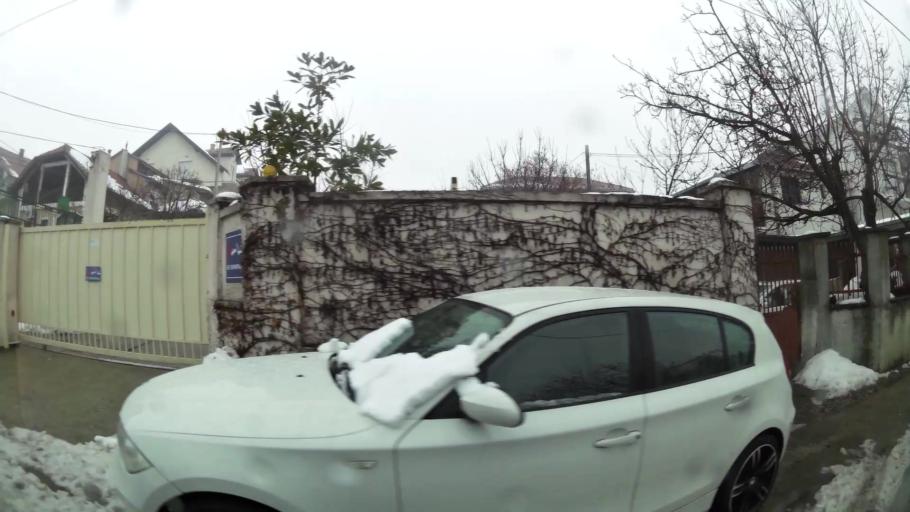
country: RS
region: Central Serbia
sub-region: Belgrade
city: Zvezdara
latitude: 44.7733
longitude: 20.5338
